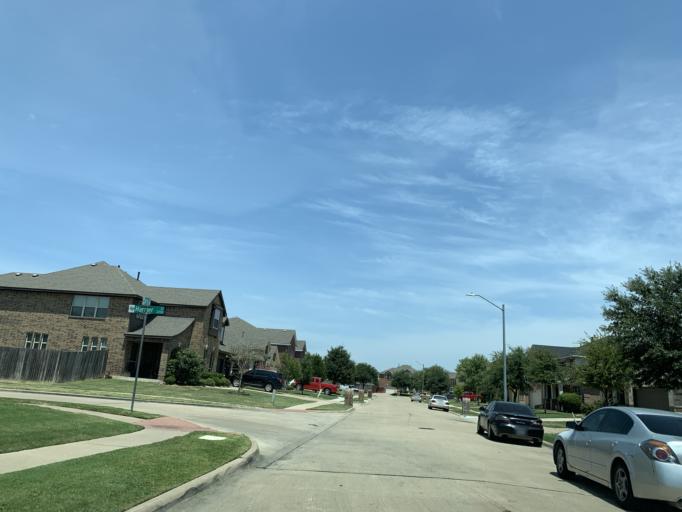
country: US
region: Texas
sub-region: Dallas County
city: Cedar Hill
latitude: 32.6510
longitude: -97.0356
